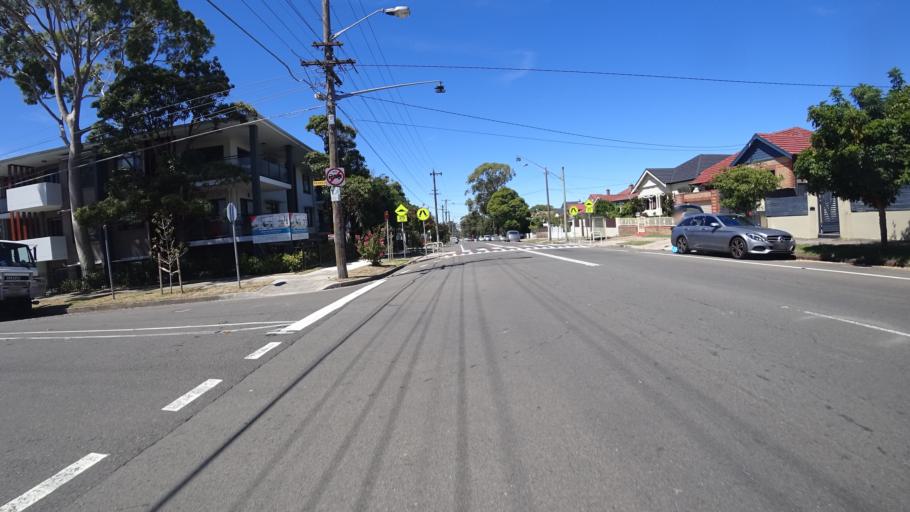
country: AU
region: New South Wales
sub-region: Rockdale
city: Bardwell Valley
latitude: -33.9404
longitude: 151.1345
